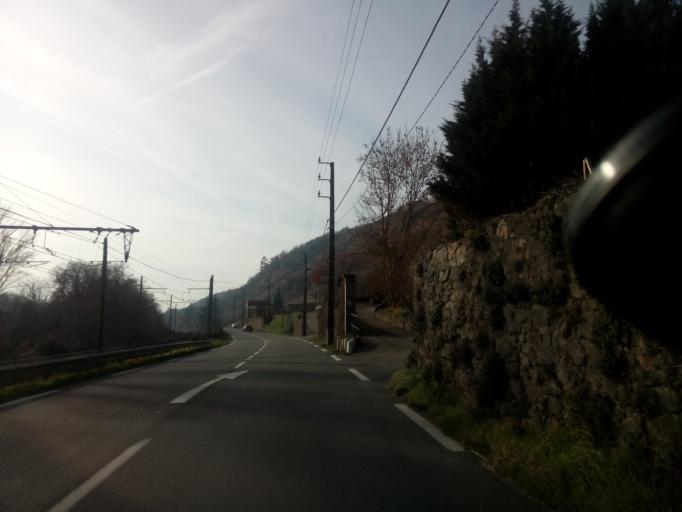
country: FR
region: Rhone-Alpes
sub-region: Departement du Rhone
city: Condrieu
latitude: 45.4811
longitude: 4.7843
